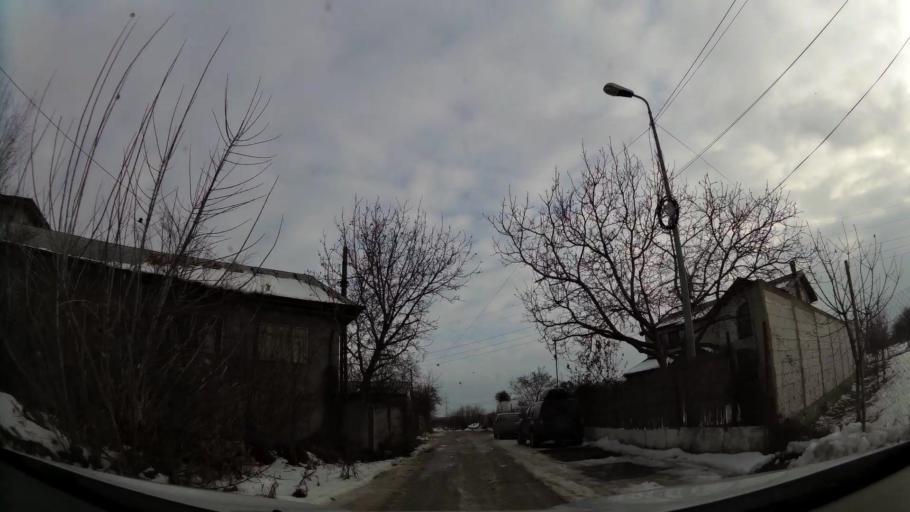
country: RO
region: Ilfov
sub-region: Comuna Popesti-Leordeni
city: Popesti-Leordeni
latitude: 44.4003
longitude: 26.1816
